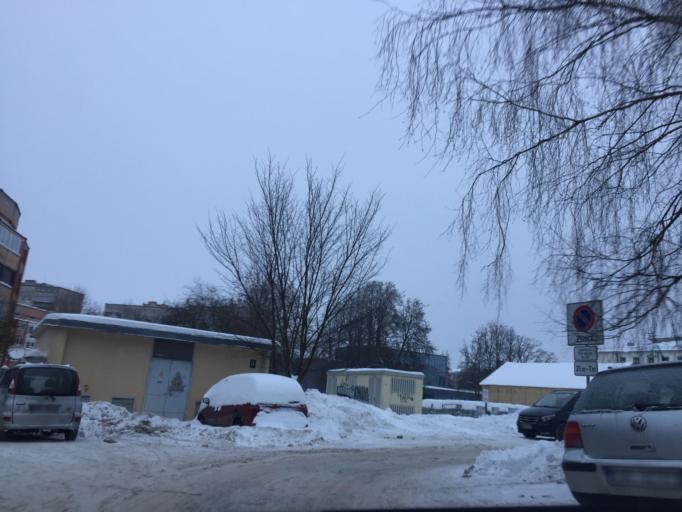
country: LV
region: Rezekne
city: Rezekne
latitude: 56.5127
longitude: 27.3309
